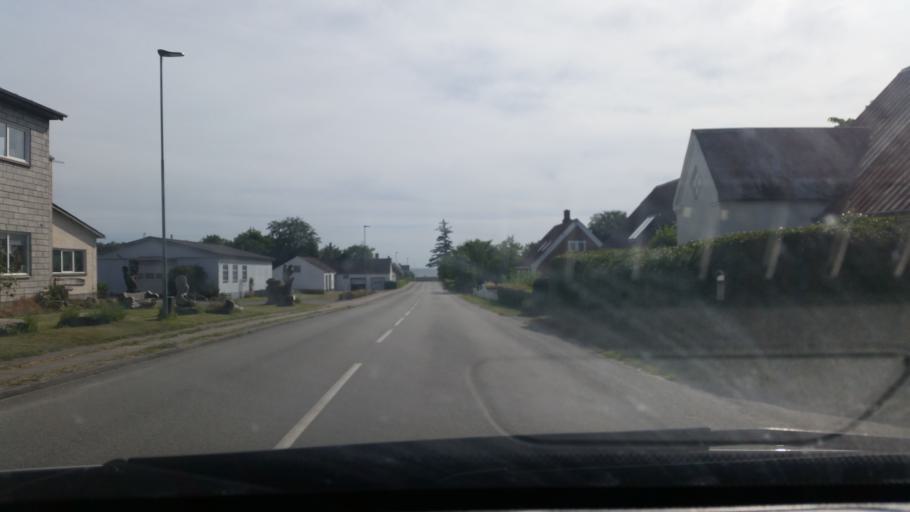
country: DK
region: Central Jutland
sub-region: Samso Kommune
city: Tranebjerg
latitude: 55.7999
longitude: 10.5350
